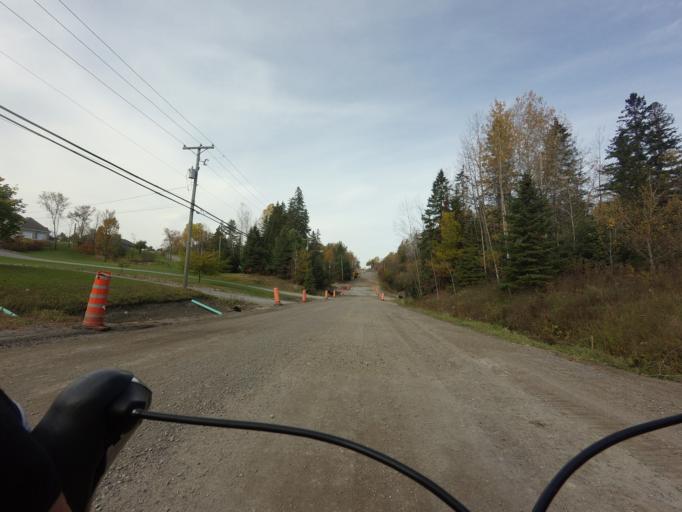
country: CA
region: Quebec
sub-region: Outaouais
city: Gatineau
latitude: 45.5212
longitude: -75.6456
